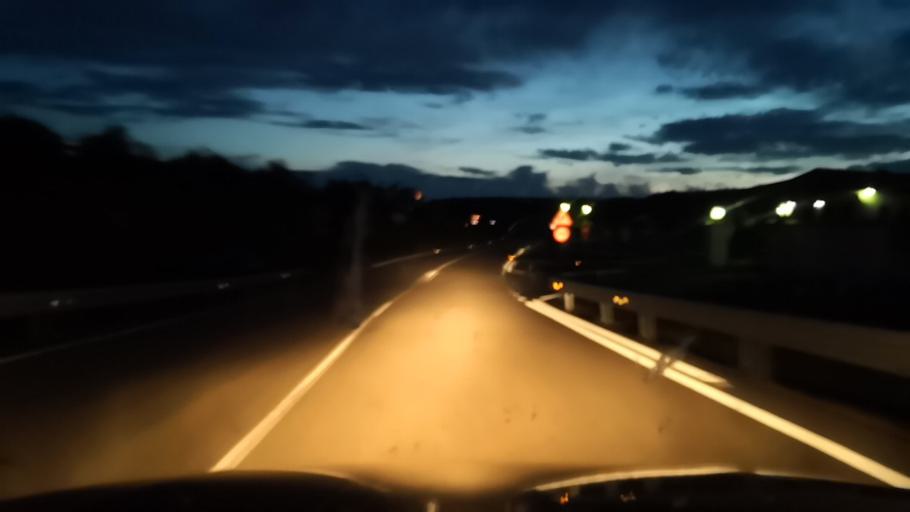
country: ES
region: Extremadura
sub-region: Provincia de Caceres
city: Plasencia
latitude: 39.9822
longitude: -6.1551
